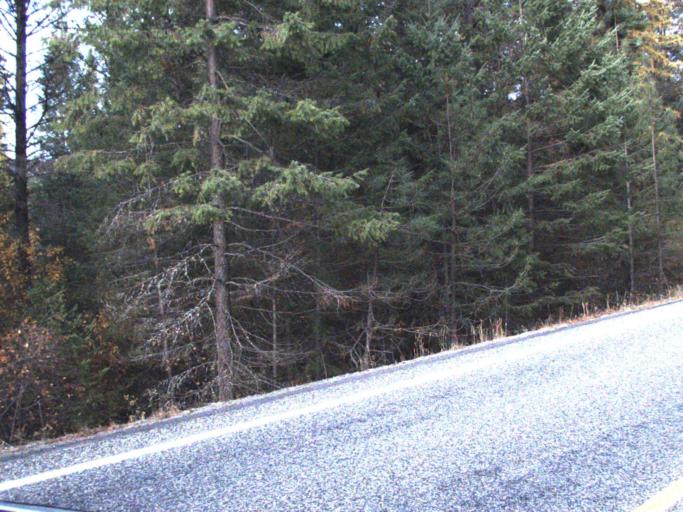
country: US
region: Washington
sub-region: Stevens County
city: Kettle Falls
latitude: 48.8134
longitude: -117.9856
